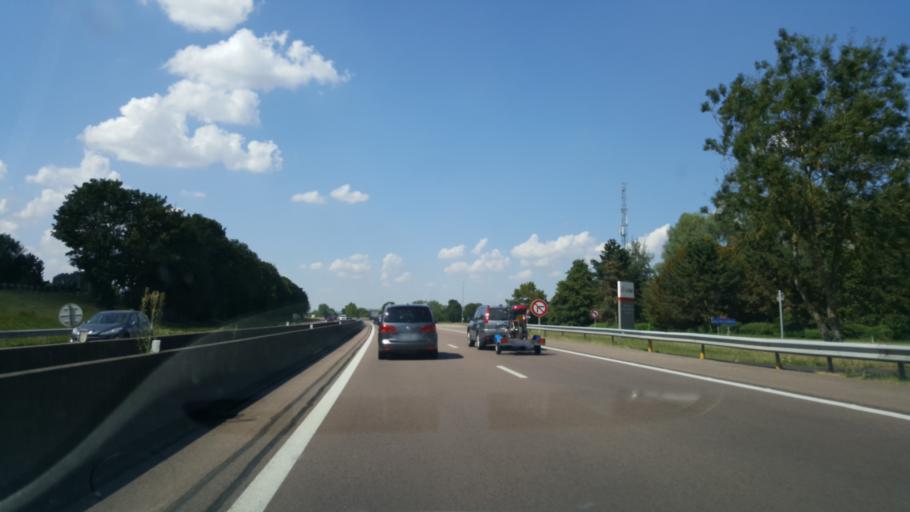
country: FR
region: Bourgogne
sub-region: Departement de la Cote-d'Or
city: Pouilly-en-Auxois
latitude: 47.3113
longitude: 4.4998
